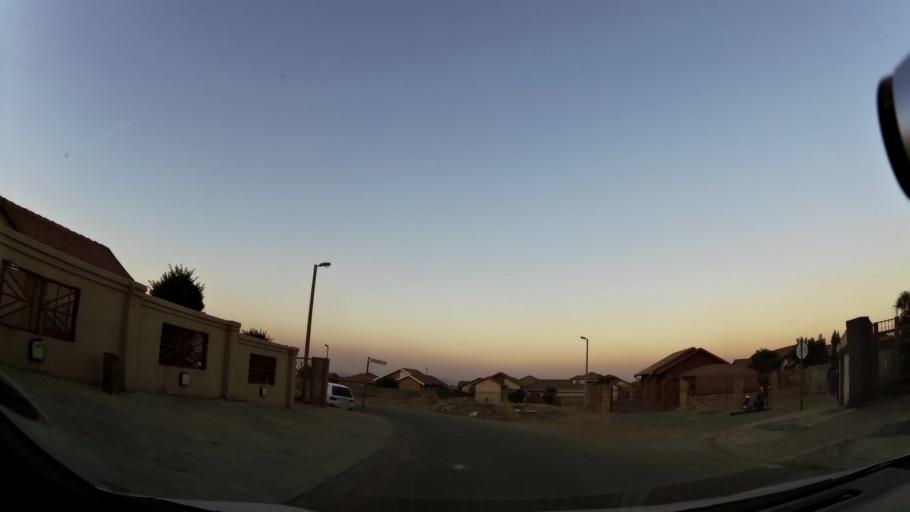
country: ZA
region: North-West
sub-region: Bojanala Platinum District Municipality
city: Rustenburg
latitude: -25.6450
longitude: 27.2034
